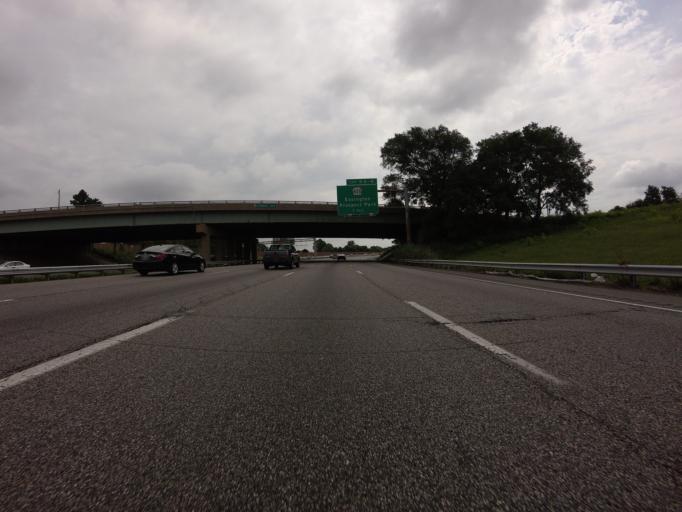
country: US
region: Pennsylvania
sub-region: Delaware County
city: Ridley Park
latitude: 39.8707
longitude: -75.3240
